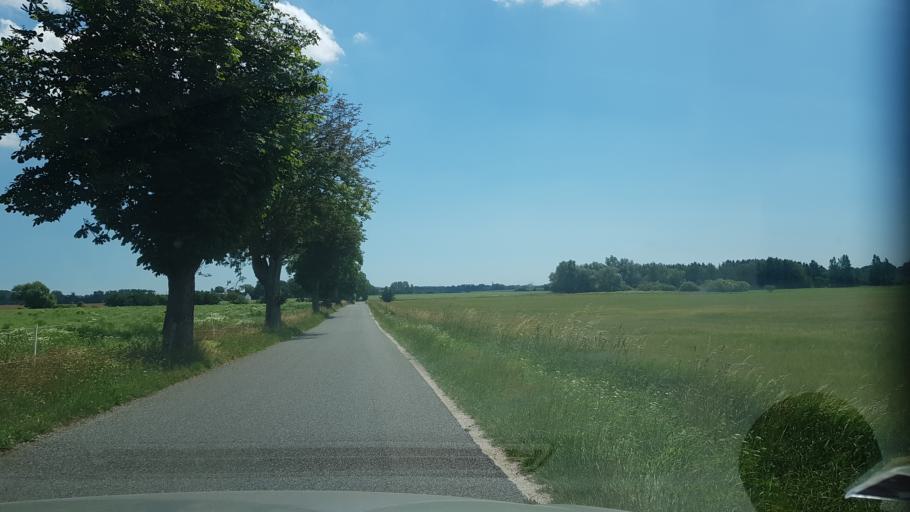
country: DK
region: Zealand
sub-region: Kalundborg Kommune
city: Svebolle
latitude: 55.7053
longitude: 11.2843
